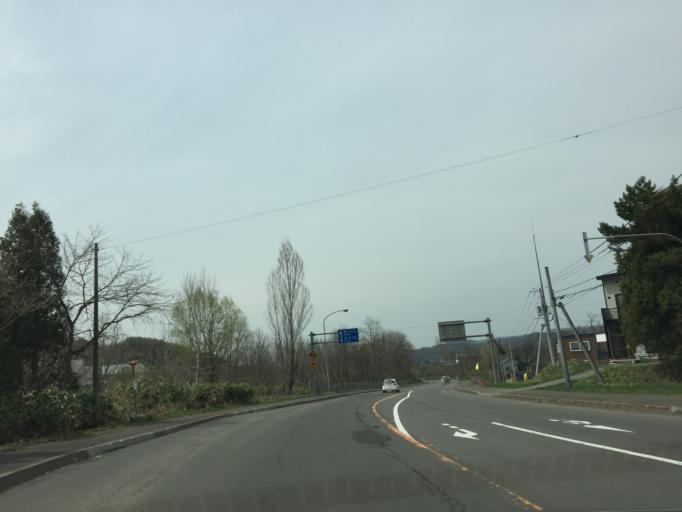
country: JP
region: Hokkaido
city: Ashibetsu
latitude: 43.5309
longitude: 142.1702
